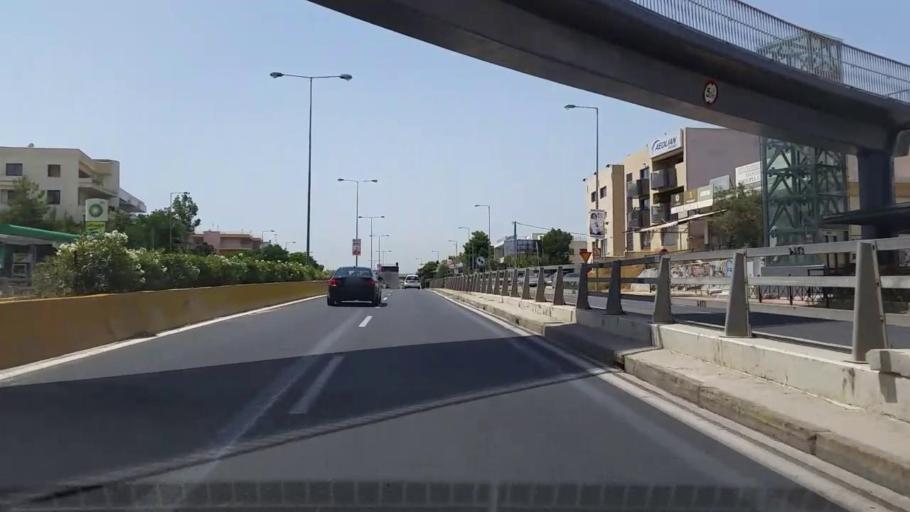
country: GR
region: Attica
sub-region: Nomarchia Athinas
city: Agia Paraskevi
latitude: 38.0114
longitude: 23.8390
